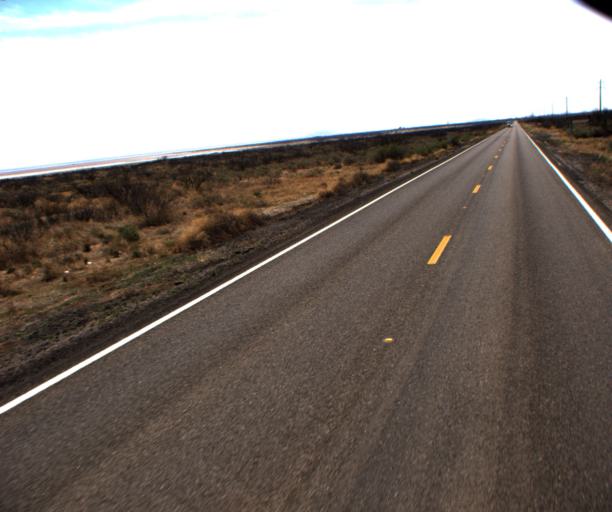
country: US
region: Arizona
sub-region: Cochise County
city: Willcox
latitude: 32.1659
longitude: -109.9441
